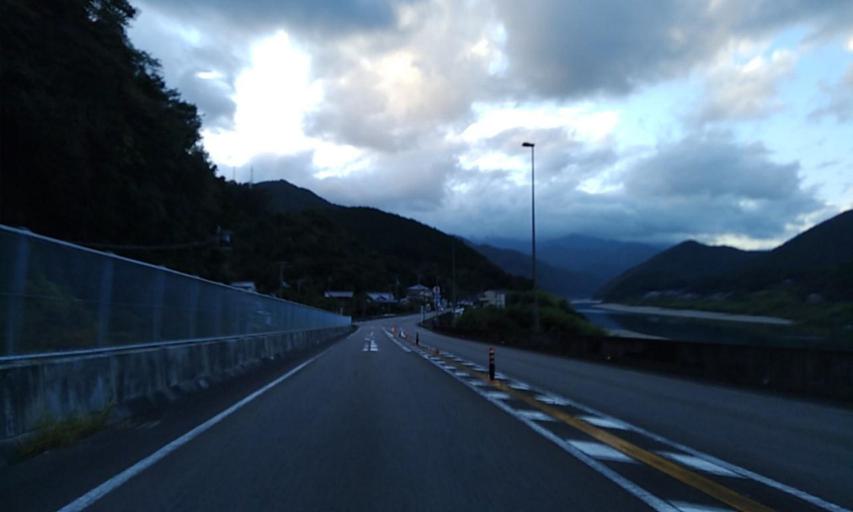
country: JP
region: Wakayama
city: Shingu
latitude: 33.7212
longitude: 135.9724
